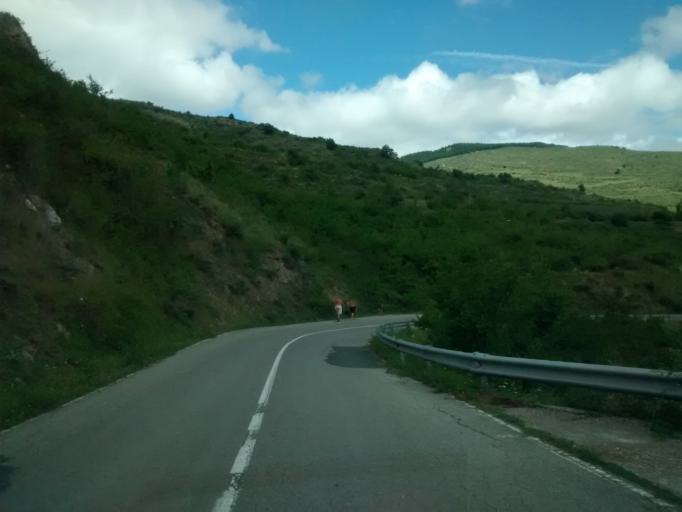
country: ES
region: La Rioja
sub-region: Provincia de La Rioja
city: Soto en Cameros
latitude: 42.2782
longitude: -2.4324
